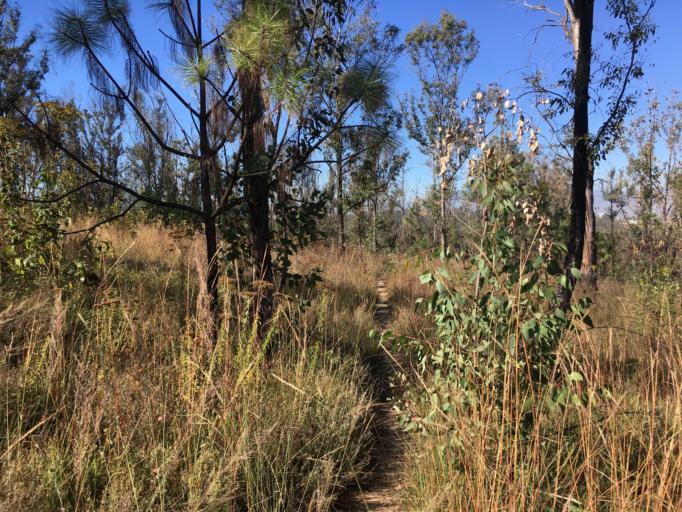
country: MX
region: Michoacan
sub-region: Morelia
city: Montana Monarca (Punta Altozano)
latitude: 19.6696
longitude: -101.1502
